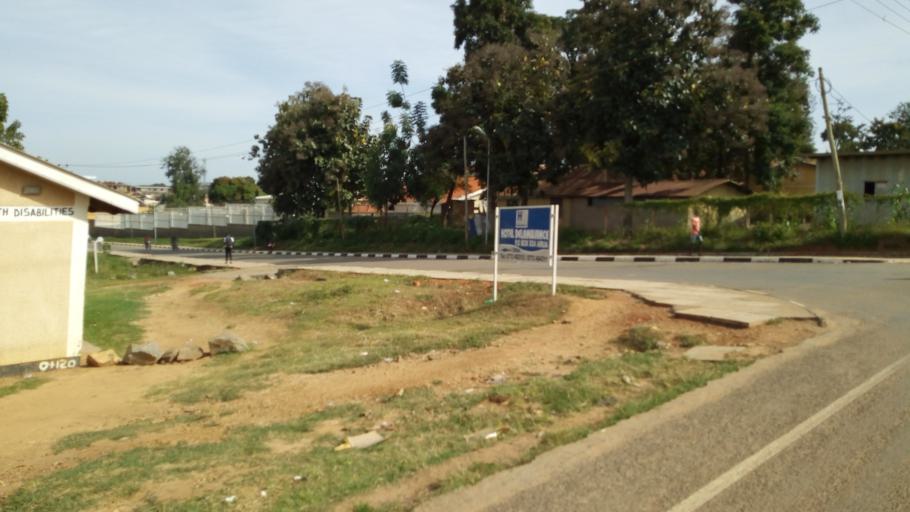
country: UG
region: Northern Region
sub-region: Arua District
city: Arua
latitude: 3.0185
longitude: 30.9112
